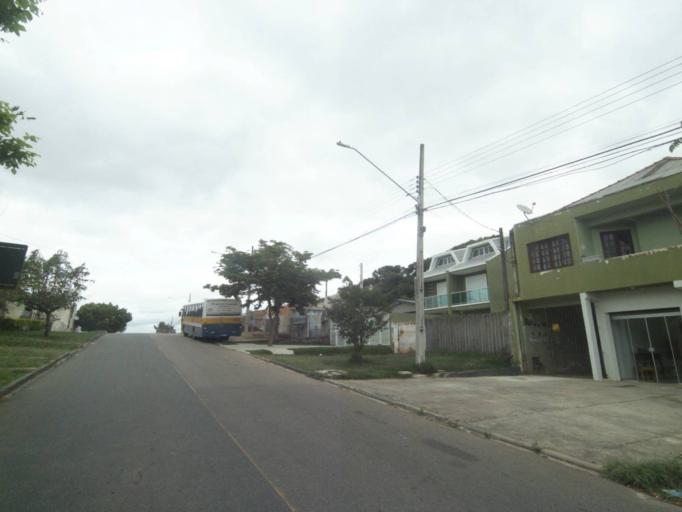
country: BR
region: Parana
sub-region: Sao Jose Dos Pinhais
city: Sao Jose dos Pinhais
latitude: -25.5558
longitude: -49.2577
